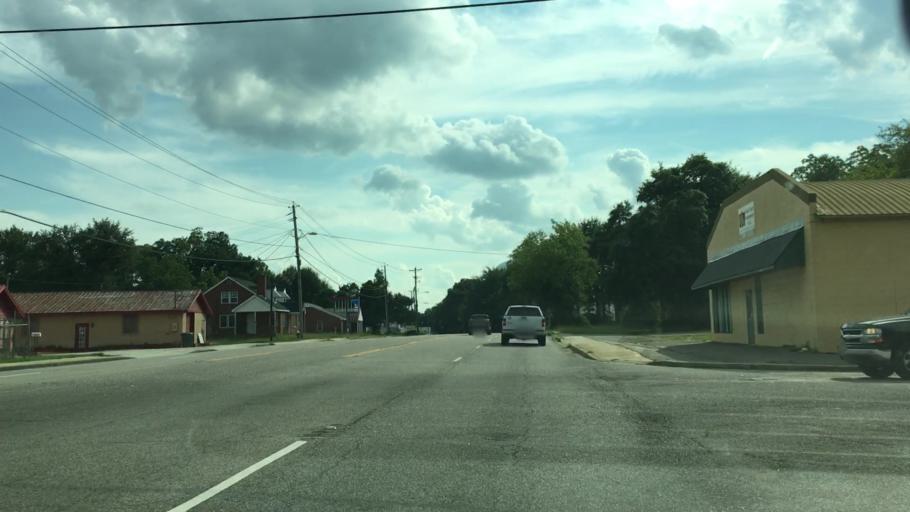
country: US
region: South Carolina
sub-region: Aiken County
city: Aiken
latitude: 33.5706
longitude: -81.7103
